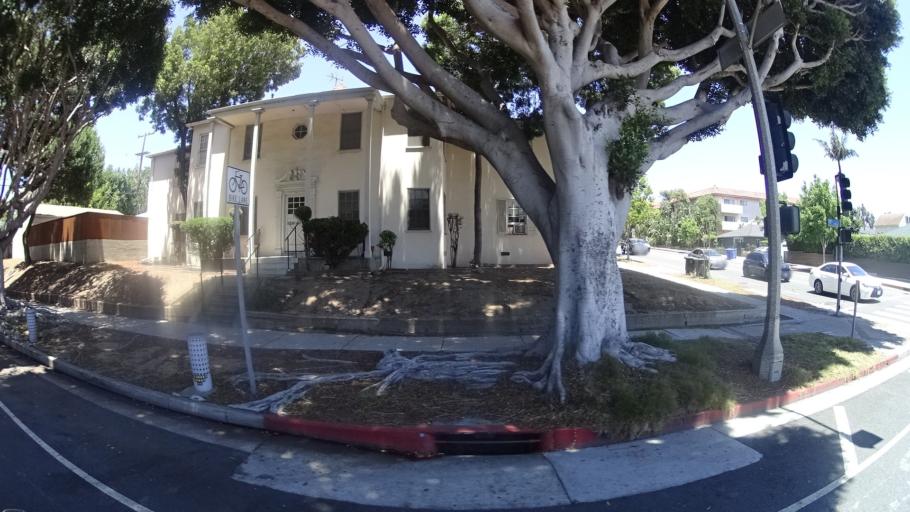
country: US
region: California
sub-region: Los Angeles County
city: Santa Monica
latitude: 34.0085
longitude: -118.4739
